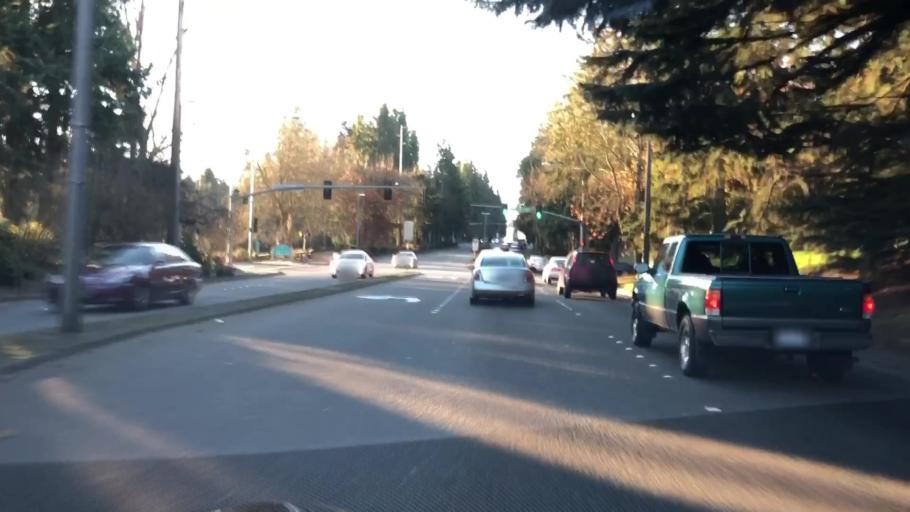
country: US
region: Washington
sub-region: King County
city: Eastgate
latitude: 47.5915
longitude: -122.1428
